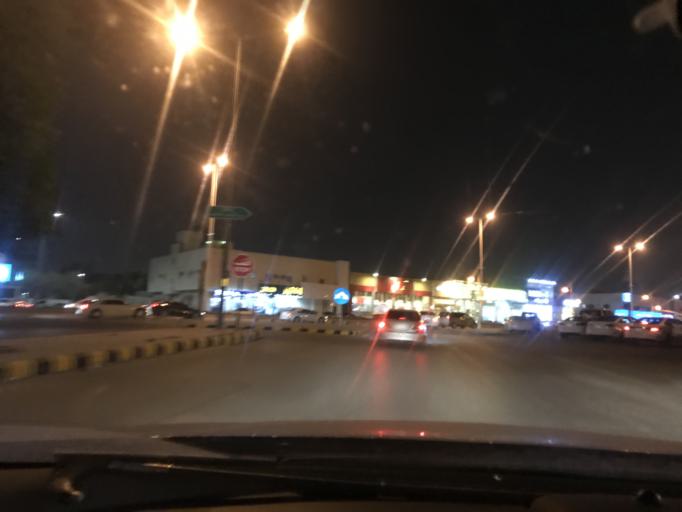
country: SA
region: Ar Riyad
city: Riyadh
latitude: 24.7466
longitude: 46.7583
